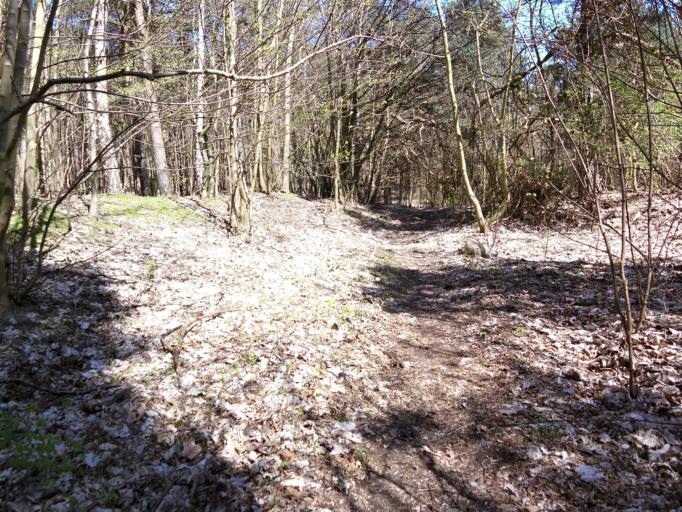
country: DE
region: Mecklenburg-Vorpommern
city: Hiddensee
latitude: 54.5939
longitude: 13.1105
